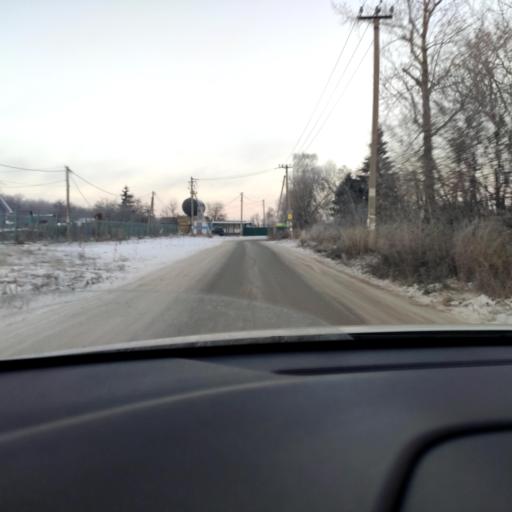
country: RU
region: Tatarstan
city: Staroye Arakchino
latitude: 55.8611
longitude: 49.0478
